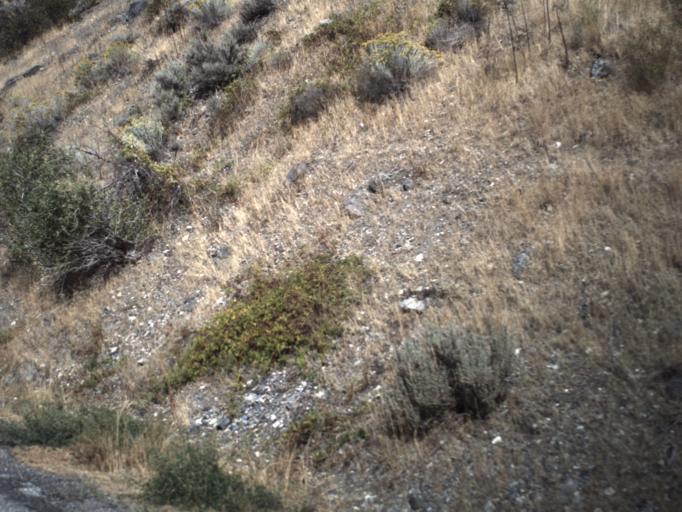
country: US
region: Utah
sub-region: Cache County
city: Hyrum
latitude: 41.6243
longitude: -111.7865
